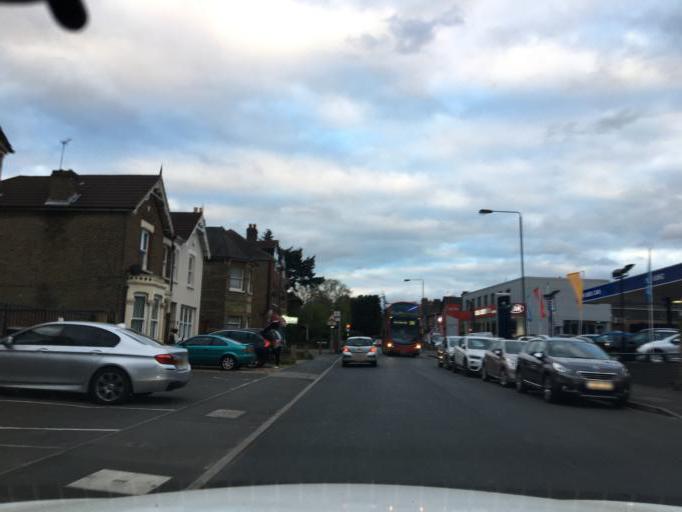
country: GB
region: England
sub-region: Greater London
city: Sidcup
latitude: 51.4295
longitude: 0.0879
